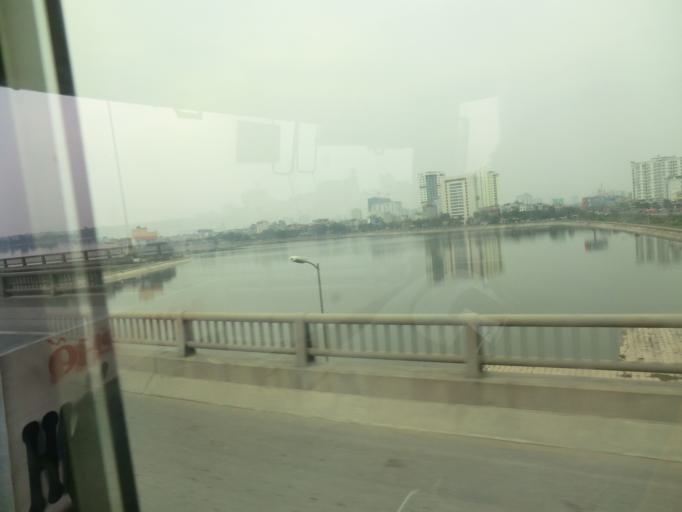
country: VN
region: Ha Noi
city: Van Dien
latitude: 20.9658
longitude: 105.8412
